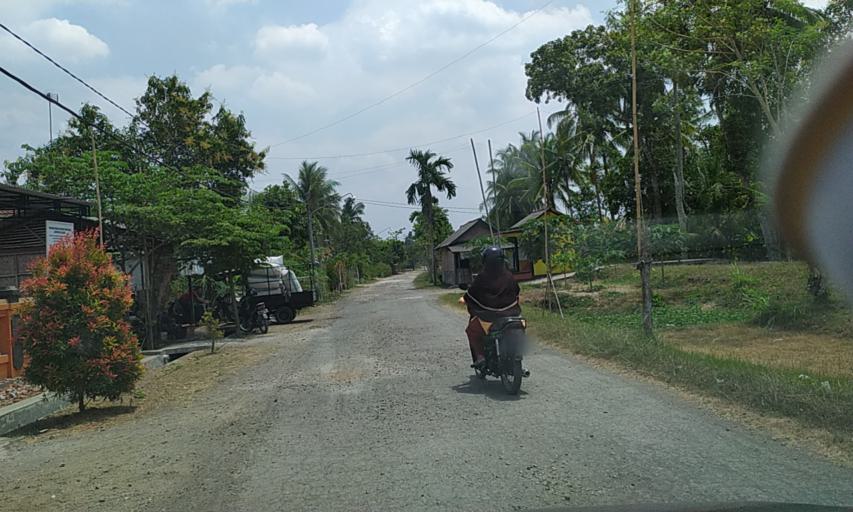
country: ID
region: Central Java
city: Kedungbakung
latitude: -7.5011
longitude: 108.7761
